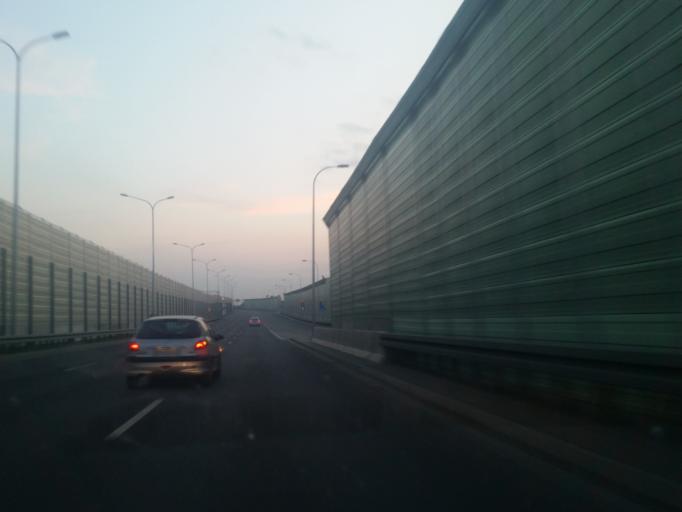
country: PL
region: Masovian Voivodeship
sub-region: Warszawa
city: Bialoleka
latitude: 52.3121
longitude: 20.9639
